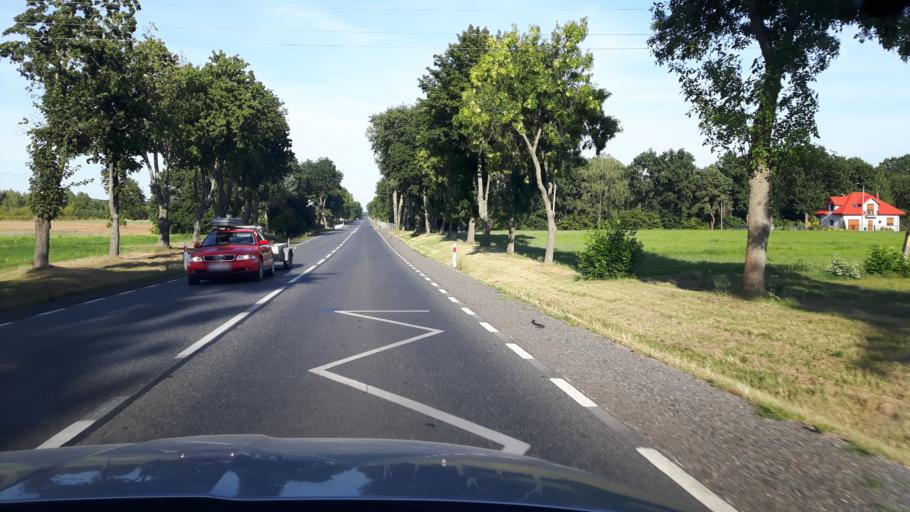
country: PL
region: Masovian Voivodeship
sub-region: Powiat nowodworski
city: Brody-Parcele
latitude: 52.4880
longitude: 20.8120
